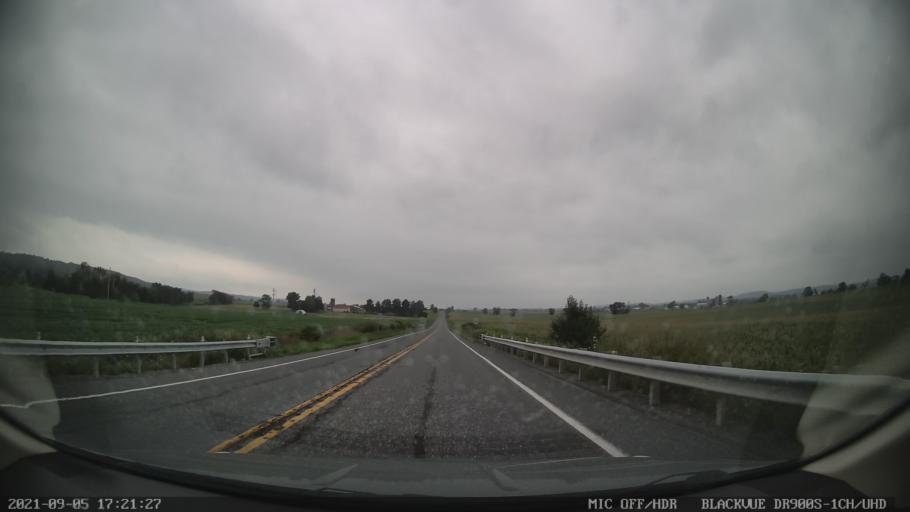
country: US
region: Pennsylvania
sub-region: Berks County
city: Kutztown
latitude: 40.4783
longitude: -75.7707
